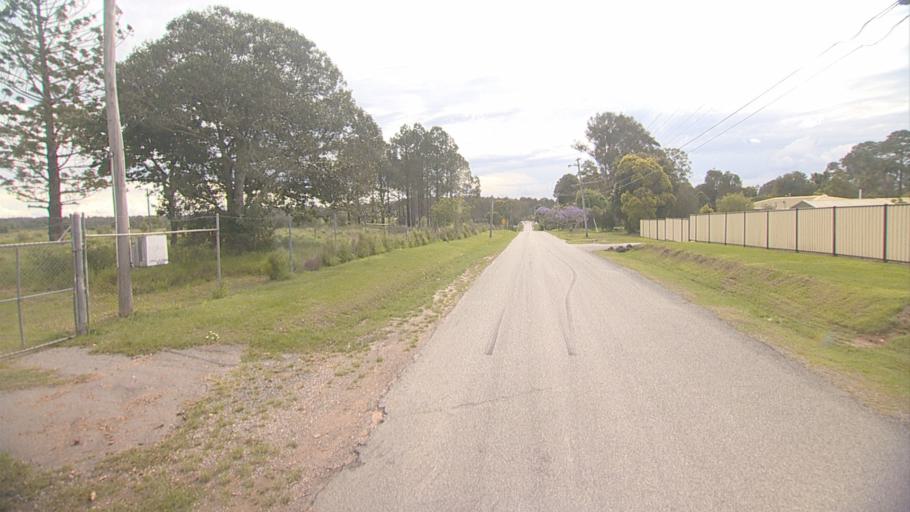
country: AU
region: Queensland
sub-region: Logan
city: Waterford West
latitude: -27.7001
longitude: 153.1226
